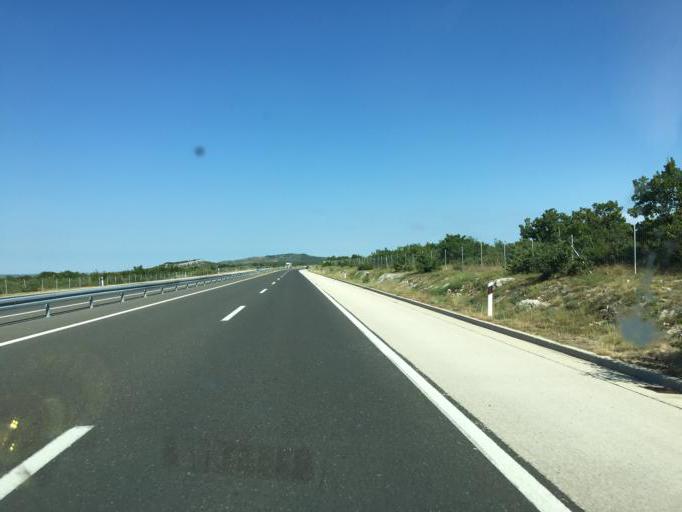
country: HR
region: Zadarska
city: Polaca
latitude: 44.0399
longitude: 15.5551
